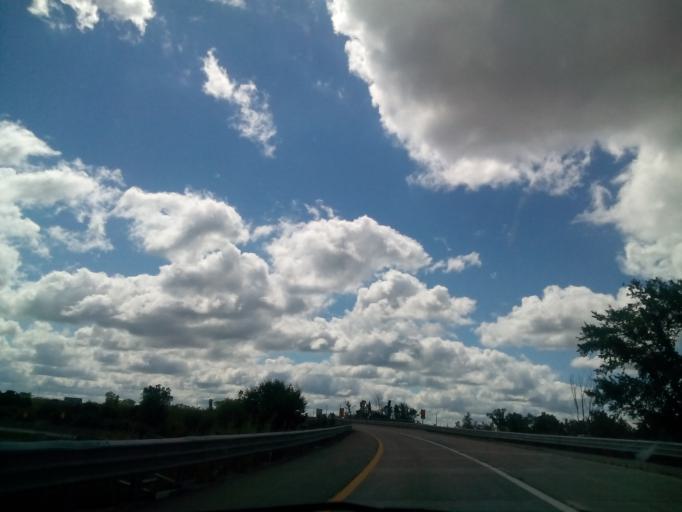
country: US
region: Michigan
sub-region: Genesee County
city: Flint
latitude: 42.9851
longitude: -83.7368
